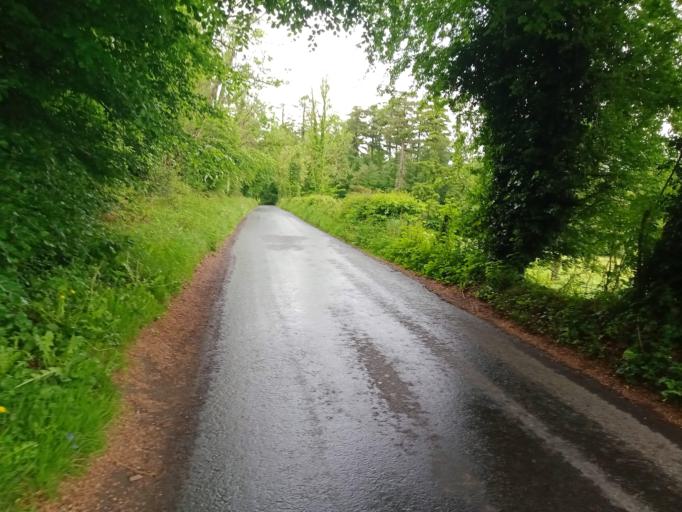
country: IE
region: Leinster
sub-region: Kilkenny
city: Thomastown
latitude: 52.4804
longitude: -7.0648
